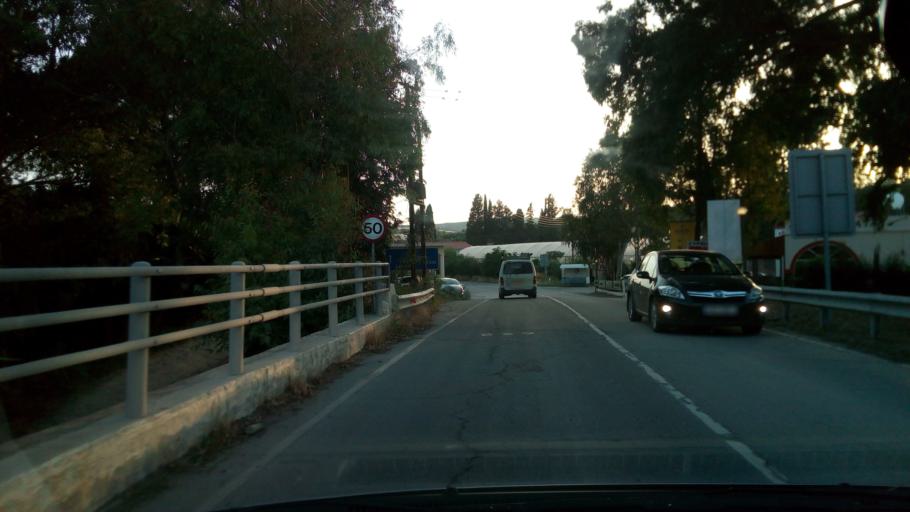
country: CY
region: Larnaka
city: Kofinou
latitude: 34.8216
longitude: 33.3758
